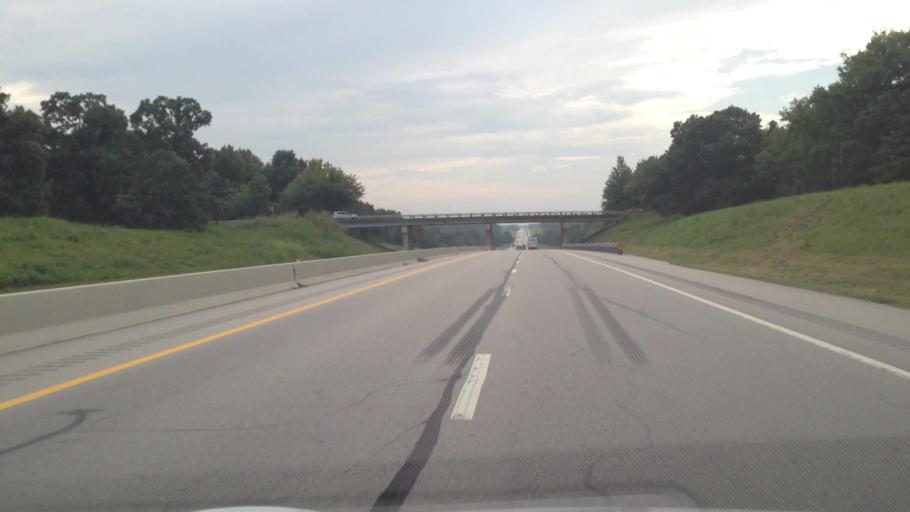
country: US
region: Kansas
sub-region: Cherokee County
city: Baxter Springs
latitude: 36.9305
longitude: -94.7258
